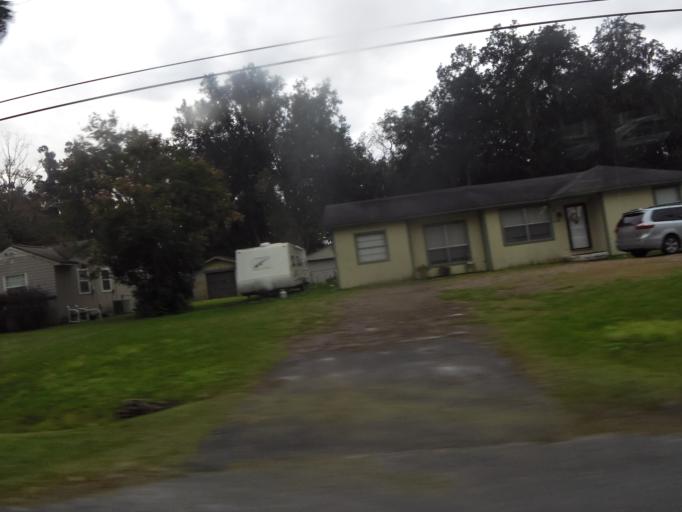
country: US
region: Florida
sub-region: Duval County
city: Jacksonville
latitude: 30.2655
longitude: -81.5944
